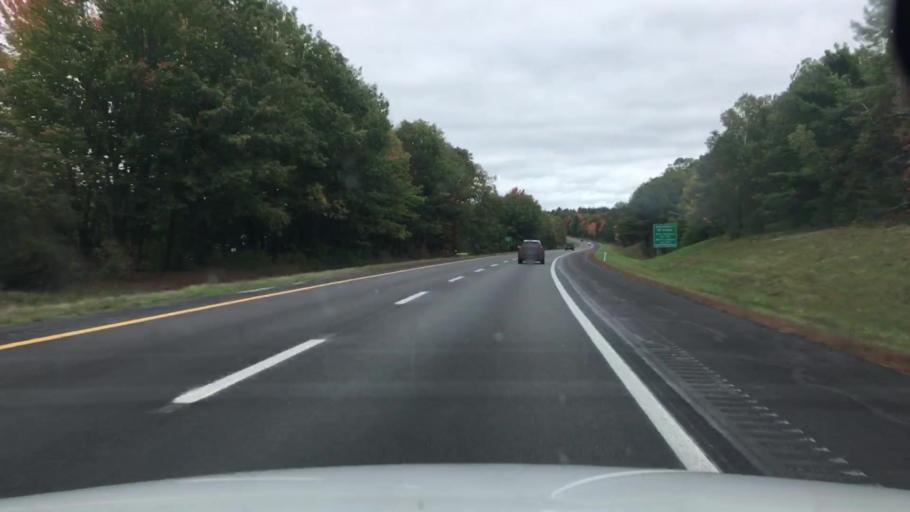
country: US
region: Maine
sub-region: Penobscot County
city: Veazie
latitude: 44.8597
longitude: -68.7179
